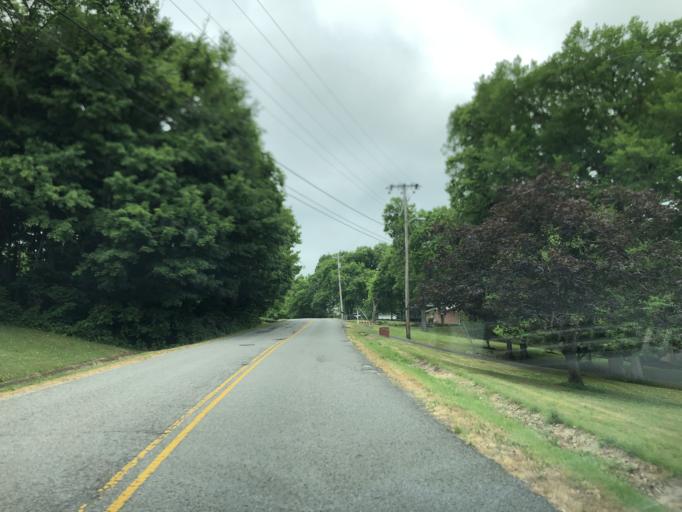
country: US
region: Tennessee
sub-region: Davidson County
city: Goodlettsville
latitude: 36.2835
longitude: -86.7361
